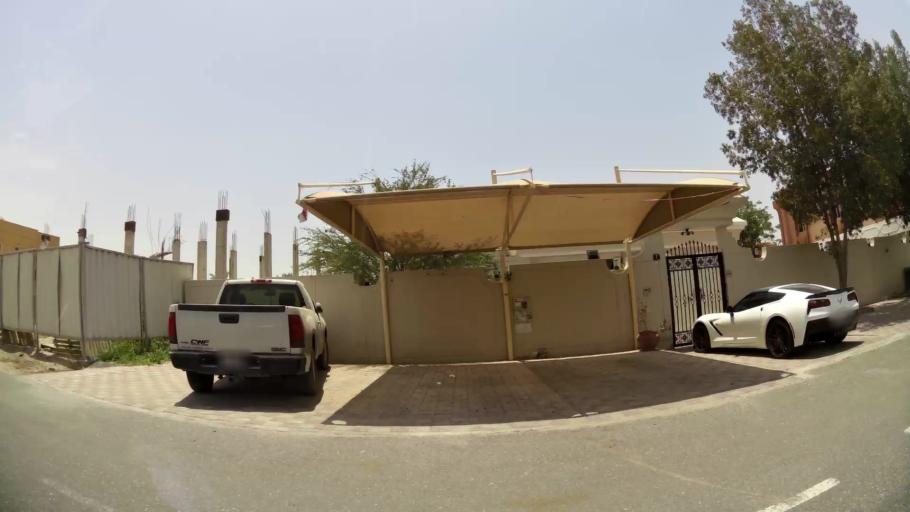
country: AE
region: Ash Shariqah
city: Sharjah
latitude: 25.1931
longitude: 55.3744
